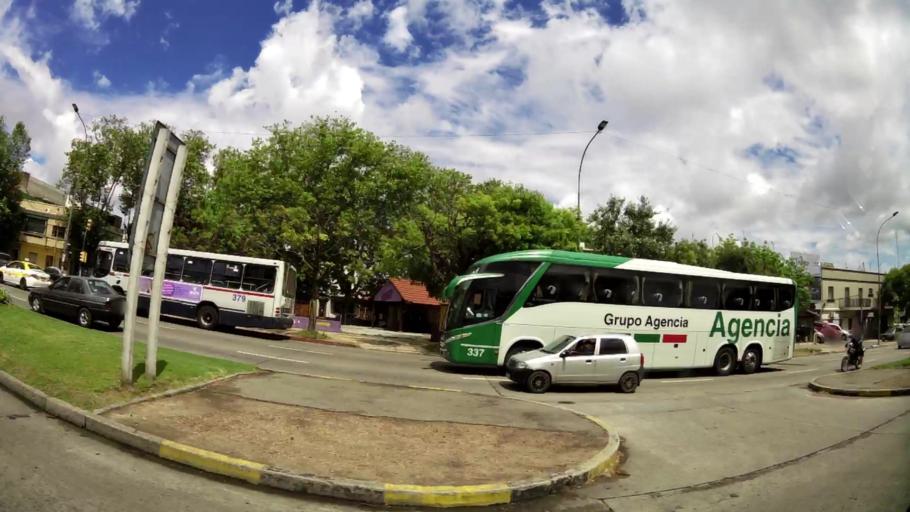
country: UY
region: Montevideo
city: Montevideo
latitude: -34.8843
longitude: -56.1659
